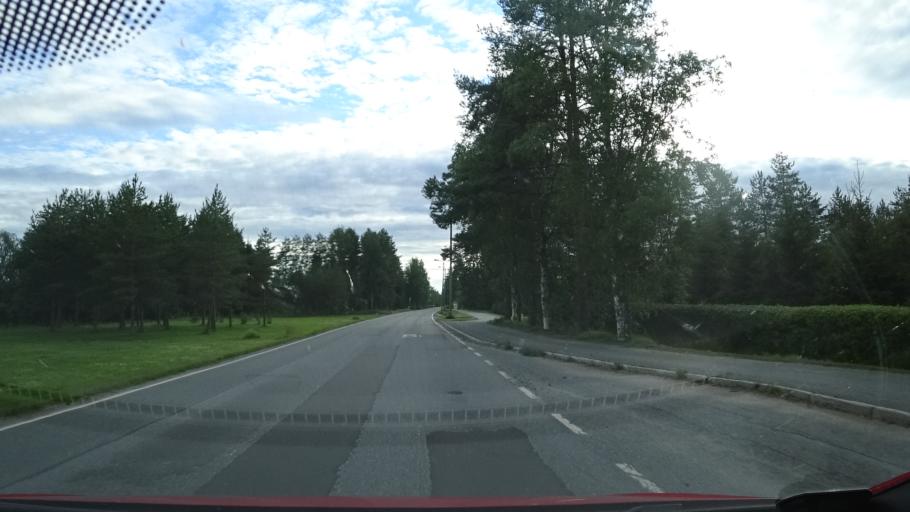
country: FI
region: Northern Ostrobothnia
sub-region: Oulu
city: Liminka
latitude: 64.8082
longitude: 25.4391
